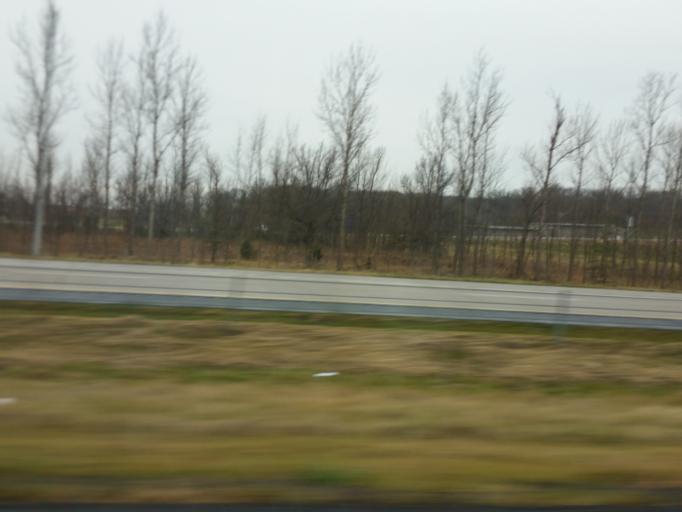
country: US
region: Iowa
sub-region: Muscatine County
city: Wilton
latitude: 41.6451
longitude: -91.1121
